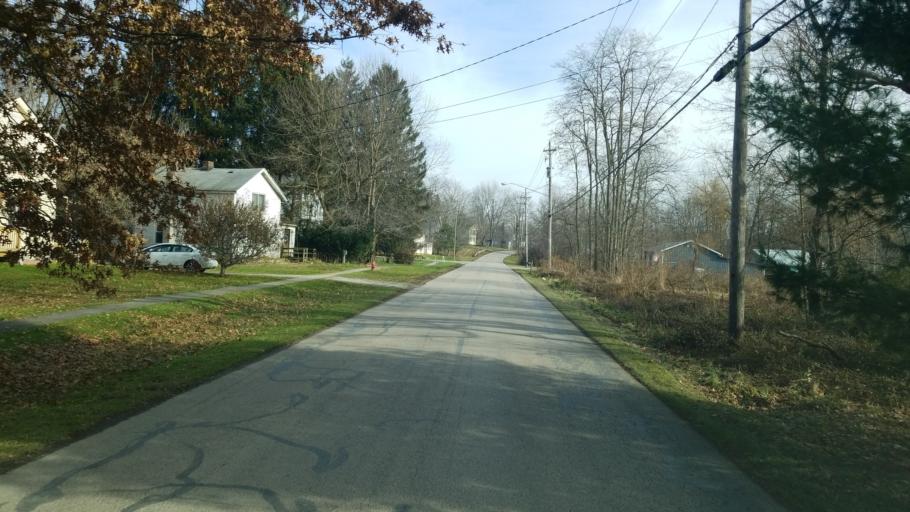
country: US
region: Ohio
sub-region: Ashtabula County
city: Roaming Shores
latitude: 41.6606
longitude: -80.8573
